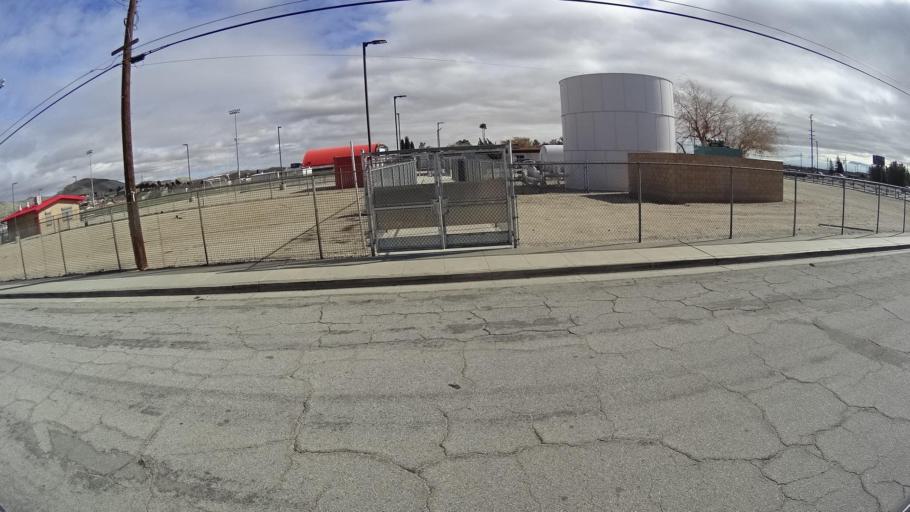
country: US
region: California
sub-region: Kern County
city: Rosamond
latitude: 34.8651
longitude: -118.1847
